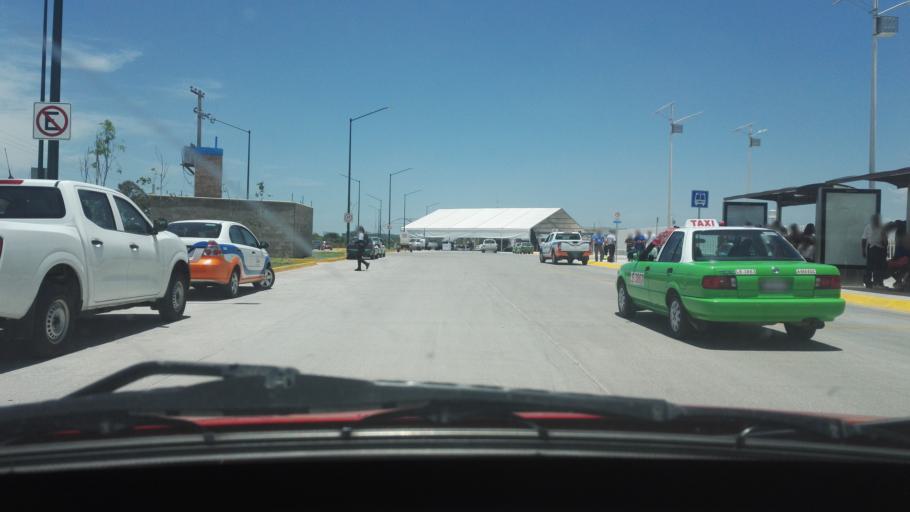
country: MX
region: Guanajuato
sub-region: Leon
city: Ladrilleras del Refugio
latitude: 21.0585
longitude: -101.5661
